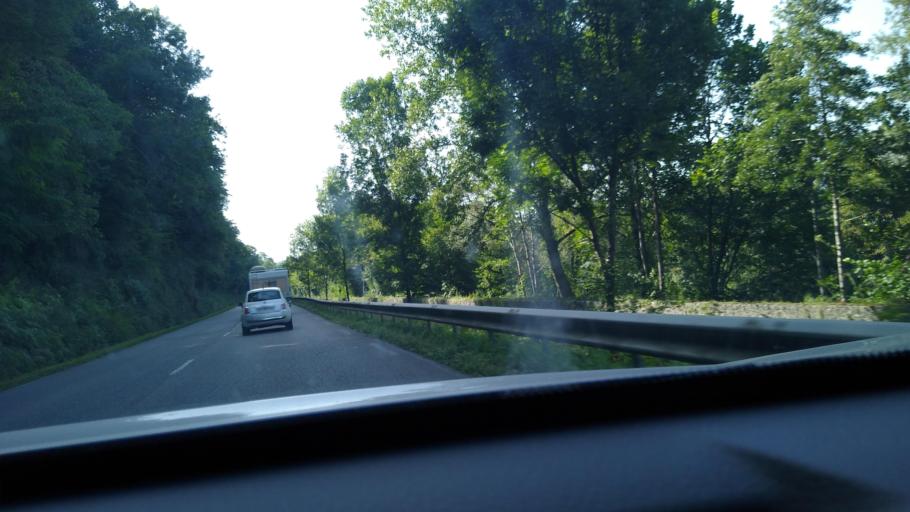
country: FR
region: Midi-Pyrenees
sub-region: Departement de l'Ariege
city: Saint-Lizier
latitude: 43.0341
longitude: 1.0752
